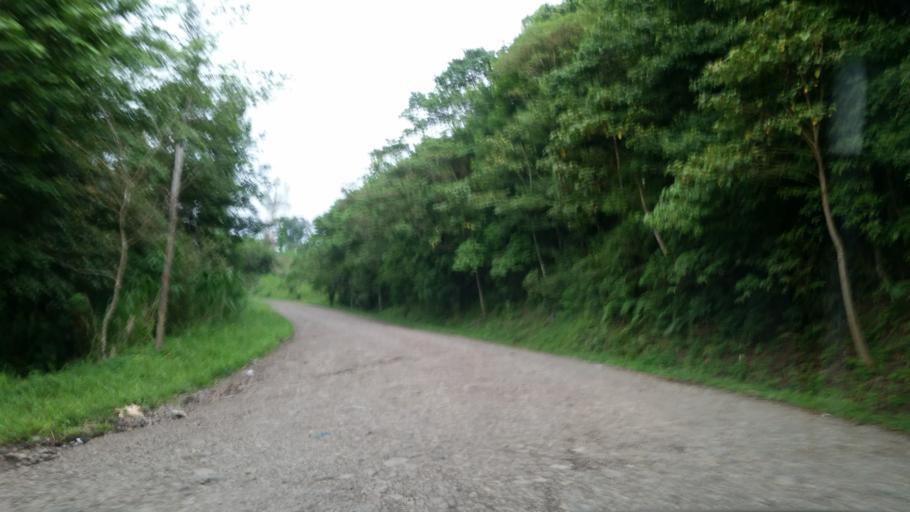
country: NI
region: Jinotega
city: San Jose de Bocay
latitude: 13.2805
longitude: -85.7206
